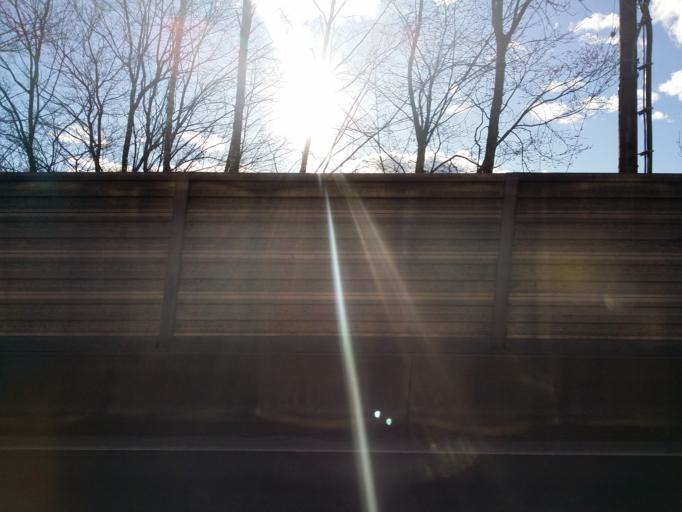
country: NO
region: Oslo
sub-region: Oslo
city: Oslo
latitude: 59.8780
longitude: 10.7759
